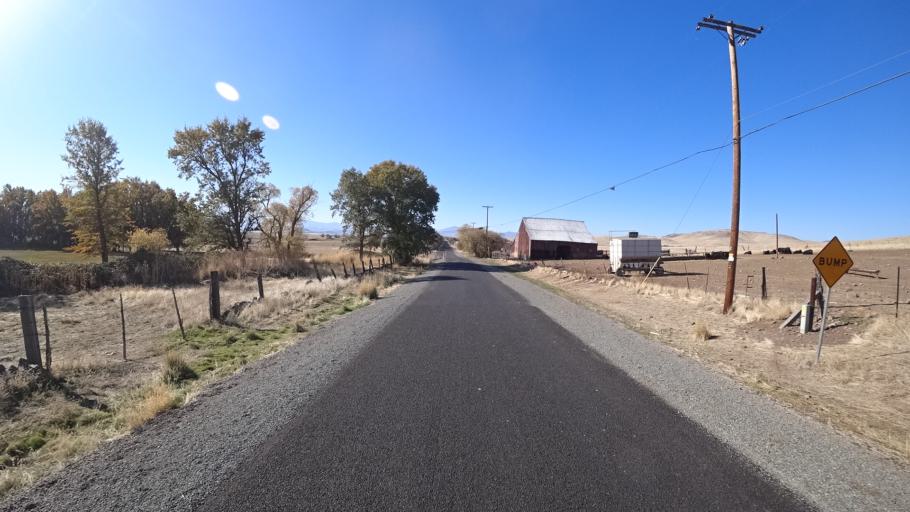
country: US
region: California
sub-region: Siskiyou County
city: Montague
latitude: 41.7263
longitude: -122.3881
